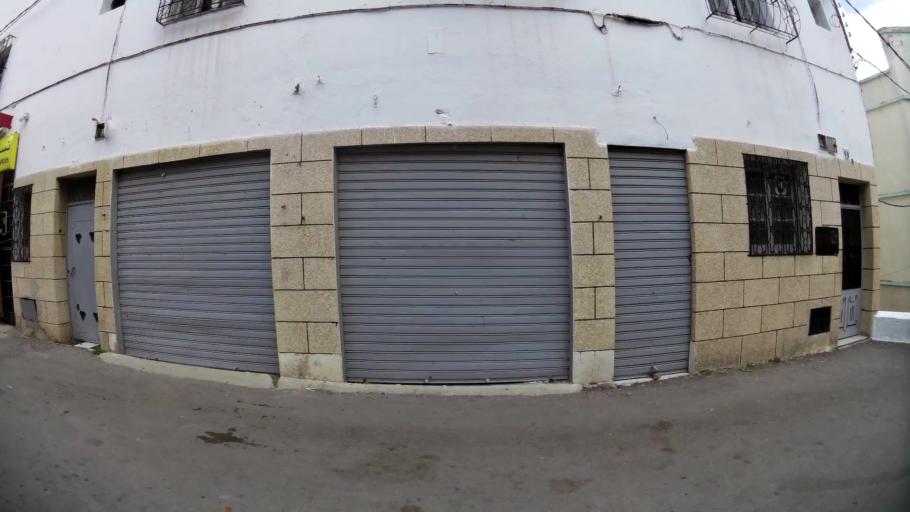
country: MA
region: Tanger-Tetouan
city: Tetouan
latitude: 35.5766
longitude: -5.3621
